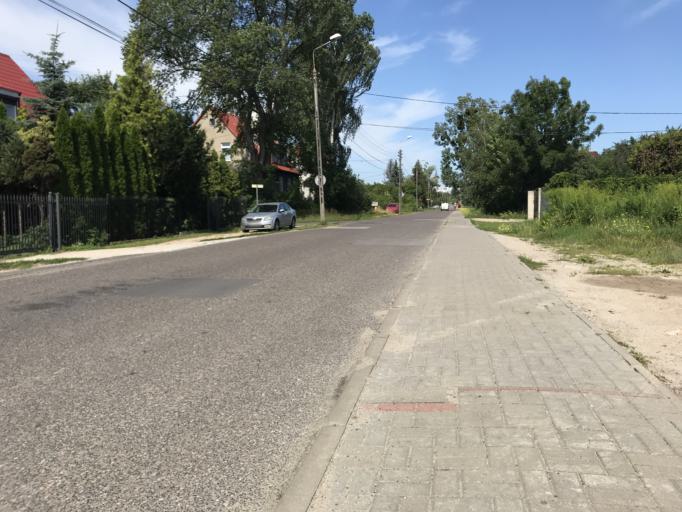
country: PL
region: Pomeranian Voivodeship
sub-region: Gdansk
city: Gdansk
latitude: 54.3379
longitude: 18.6742
